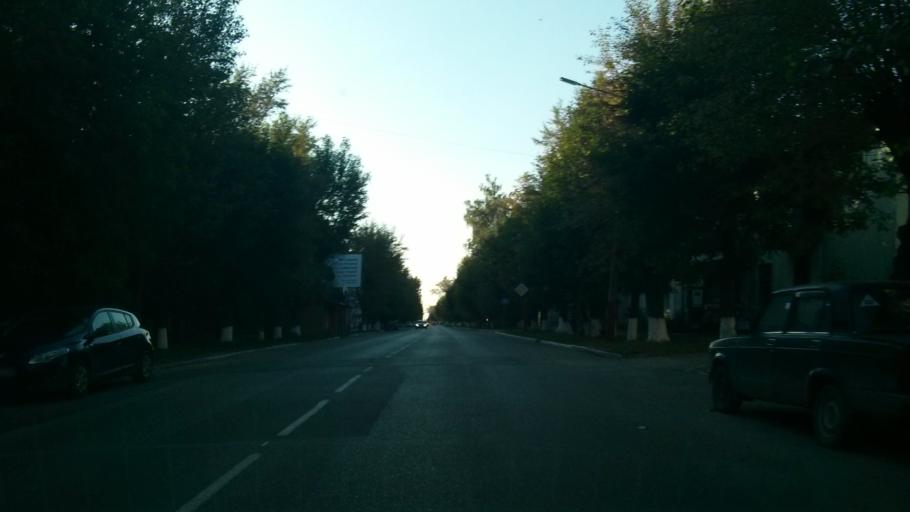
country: RU
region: Vladimir
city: Murom
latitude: 55.5649
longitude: 42.0579
